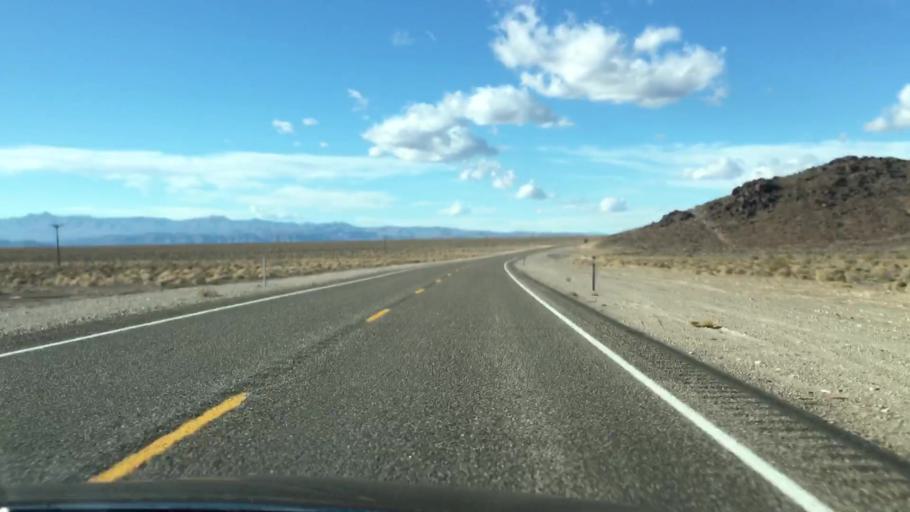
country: US
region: Nevada
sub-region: Nye County
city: Beatty
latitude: 37.1797
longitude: -116.9310
